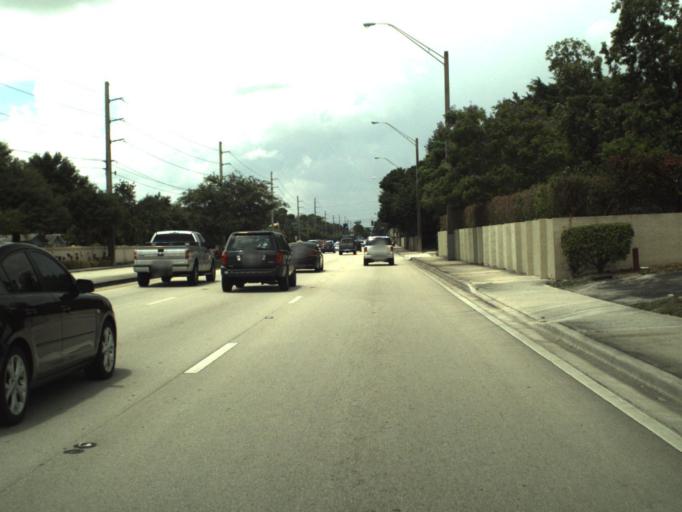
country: US
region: Florida
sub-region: Broward County
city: Dania Beach
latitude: 26.0474
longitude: -80.1883
